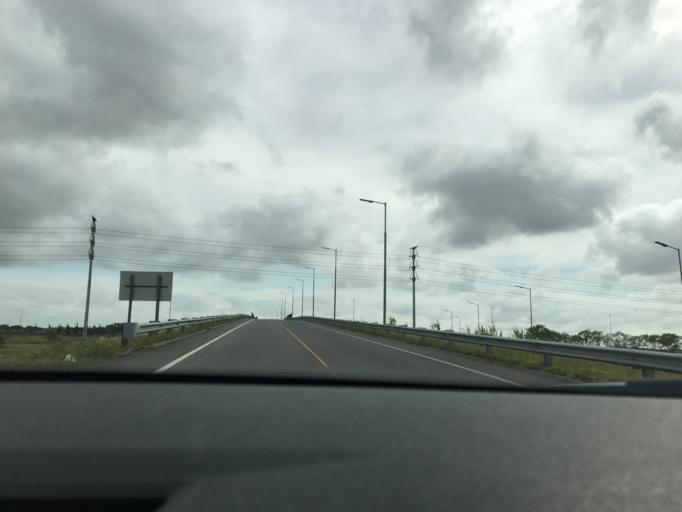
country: AR
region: Buenos Aires
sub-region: Partido de La Plata
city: La Plata
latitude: -34.8404
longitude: -58.0715
